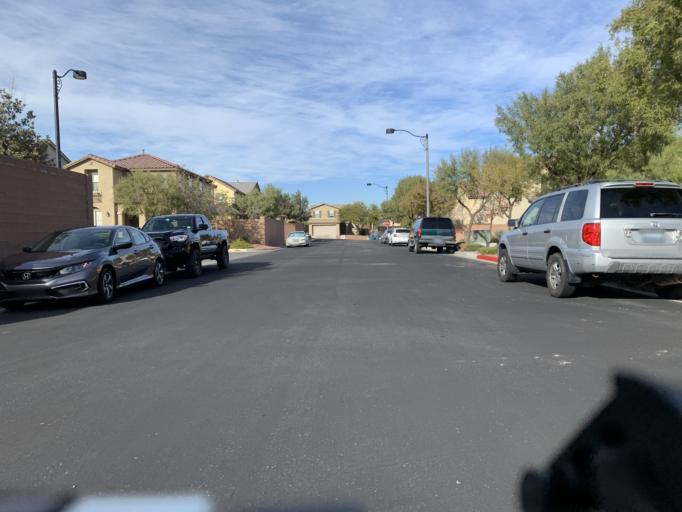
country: US
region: Nevada
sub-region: Clark County
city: Summerlin South
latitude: 36.2978
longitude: -115.3319
